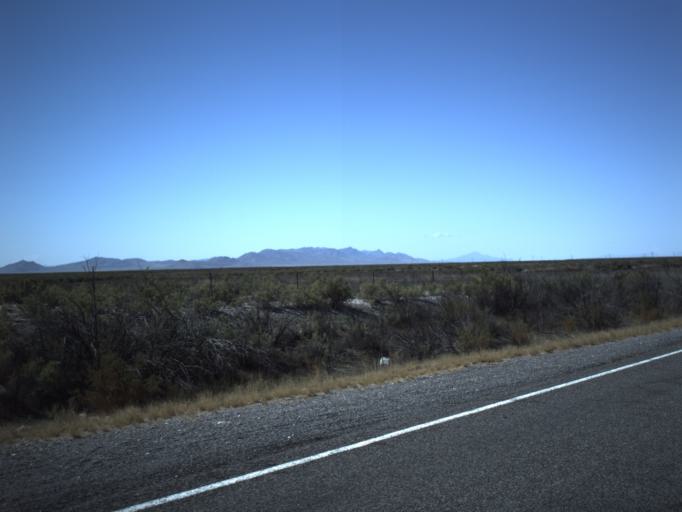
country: US
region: Utah
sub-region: Millard County
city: Delta
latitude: 39.2730
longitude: -112.8585
